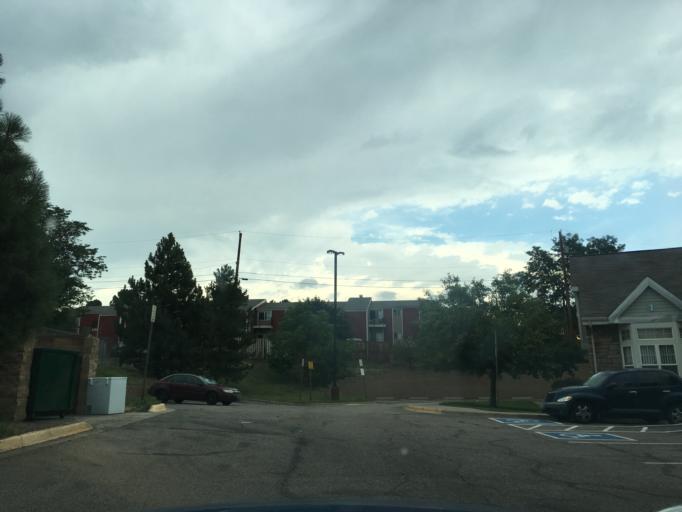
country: US
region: Colorado
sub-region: Arapahoe County
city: Sheridan
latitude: 39.6563
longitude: -105.0284
